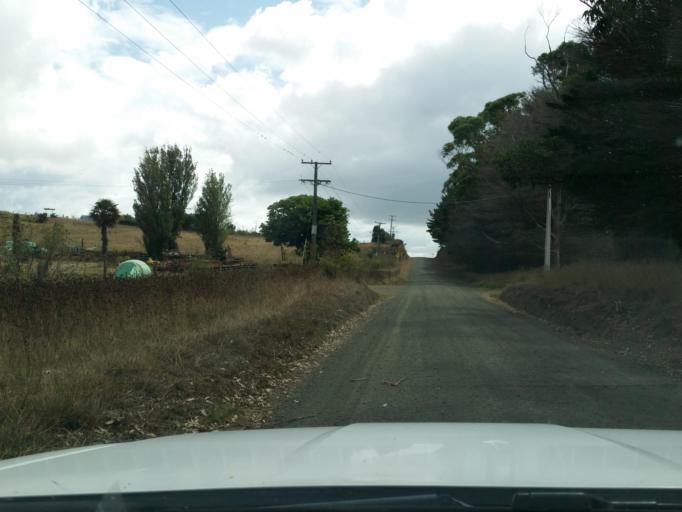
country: NZ
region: Auckland
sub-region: Auckland
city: Wellsford
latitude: -36.3552
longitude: 174.1746
